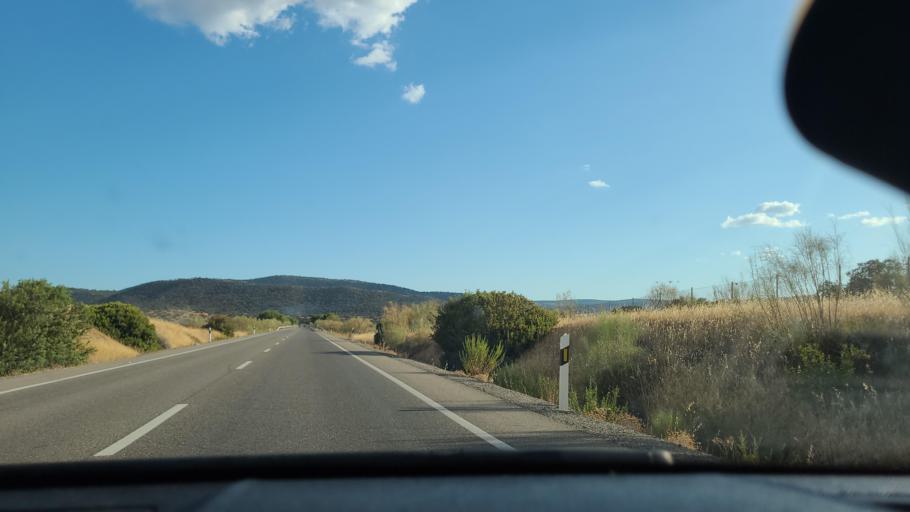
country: ES
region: Andalusia
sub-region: Province of Cordoba
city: Belmez
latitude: 38.2432
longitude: -5.1674
